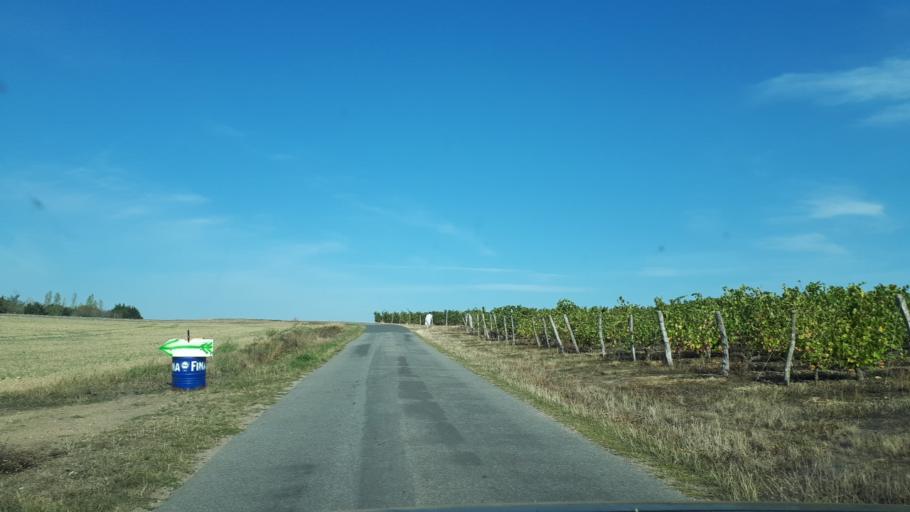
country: FR
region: Centre
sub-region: Departement du Loir-et-Cher
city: Villiers-sur-Loir
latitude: 47.8274
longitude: 0.9646
